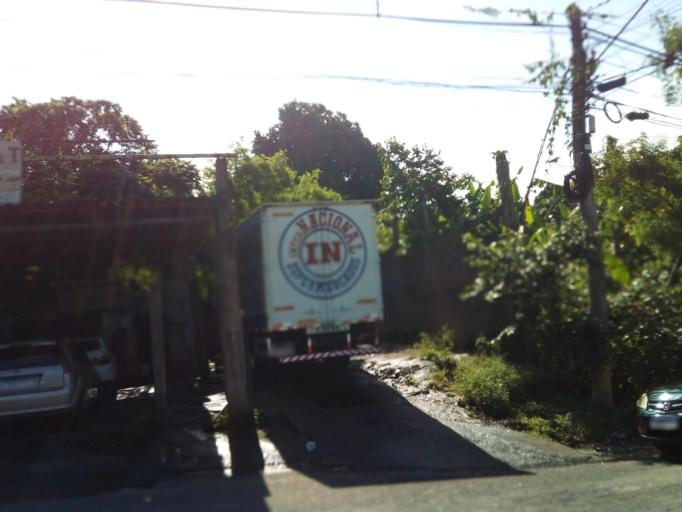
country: BR
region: Espirito Santo
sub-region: Vitoria
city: Vitoria
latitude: -20.2958
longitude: -40.3755
